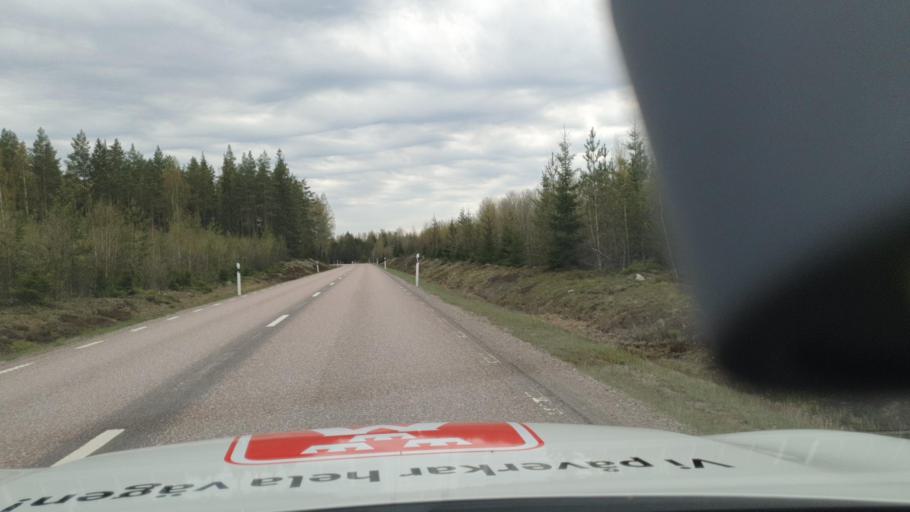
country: SE
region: Gaevleborg
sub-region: Gavle Kommun
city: Hedesunda
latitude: 60.3043
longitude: 16.9145
